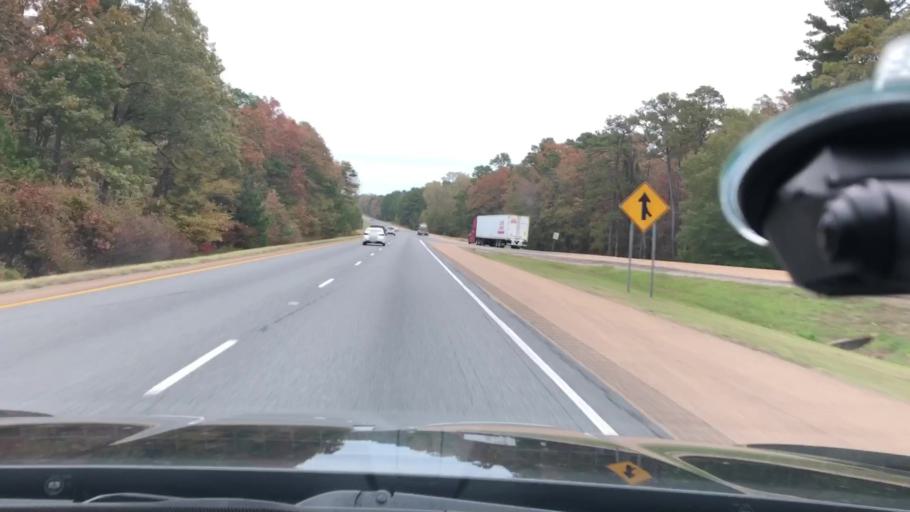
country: US
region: Arkansas
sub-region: Clark County
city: Gurdon
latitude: 33.9305
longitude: -93.2590
